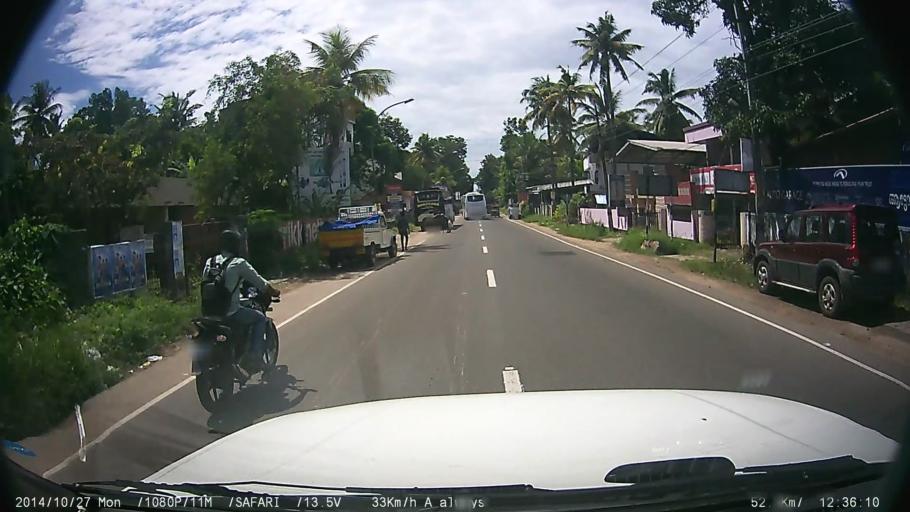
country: IN
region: Kerala
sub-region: Kottayam
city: Changanacheri
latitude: 9.4381
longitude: 76.5438
